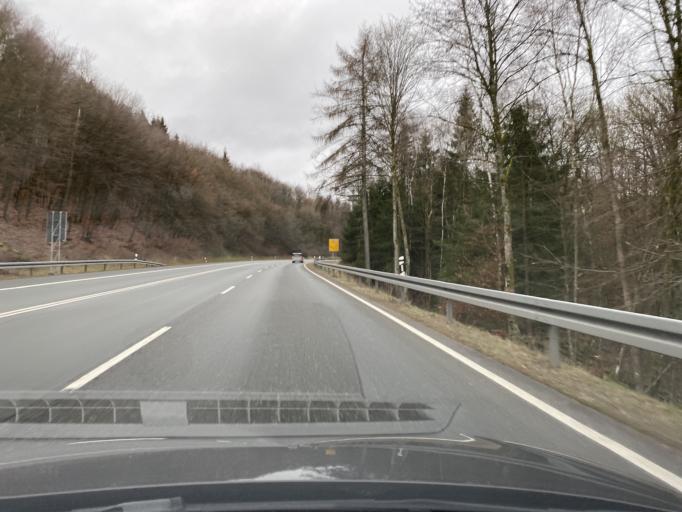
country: DE
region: North Rhine-Westphalia
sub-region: Regierungsbezirk Arnsberg
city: Meschede
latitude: 51.3809
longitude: 8.2966
